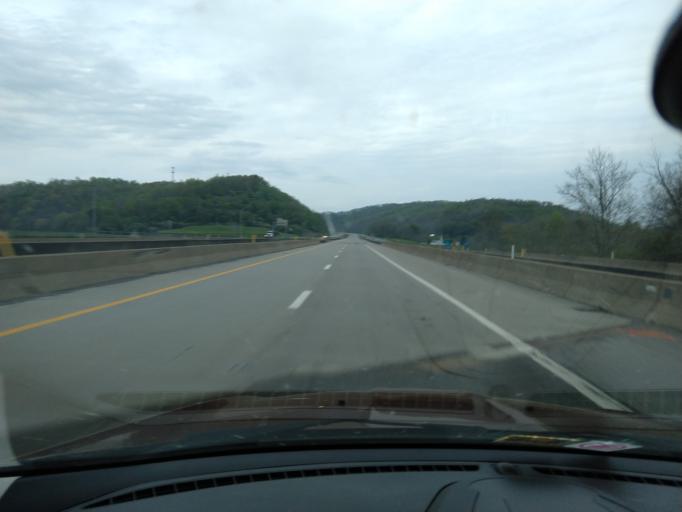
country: US
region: West Virginia
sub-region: Lewis County
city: Weston
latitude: 39.0193
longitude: -80.4292
